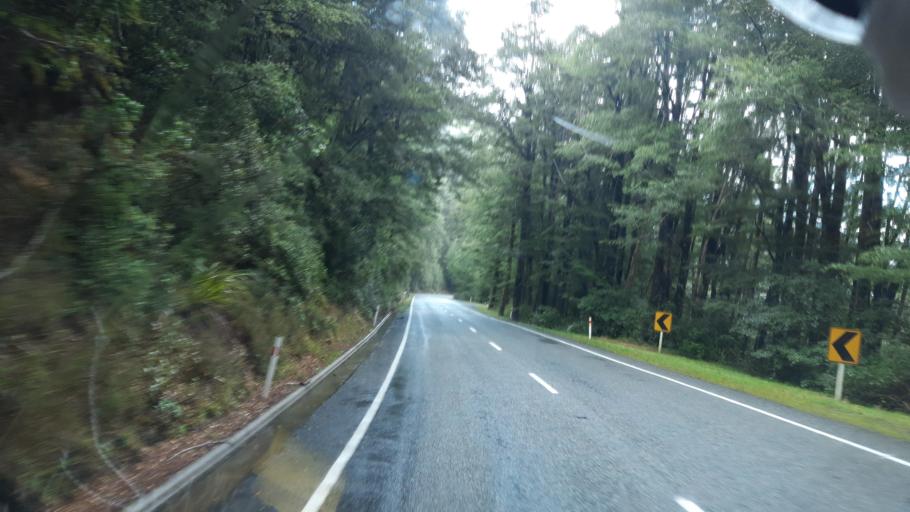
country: NZ
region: Canterbury
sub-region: Hurunui District
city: Amberley
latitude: -42.3780
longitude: 172.3467
